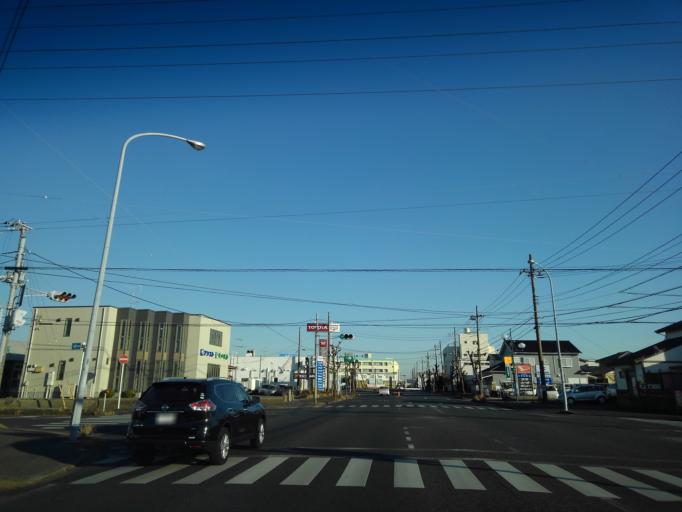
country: JP
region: Chiba
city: Kimitsu
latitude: 35.3183
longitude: 139.9199
